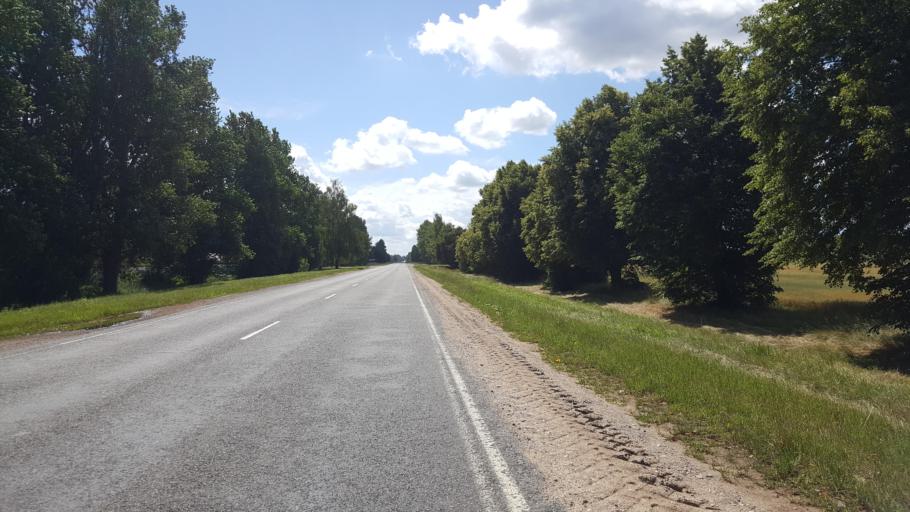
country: BY
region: Brest
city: Kamyanyets
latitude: 52.3586
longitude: 23.8933
